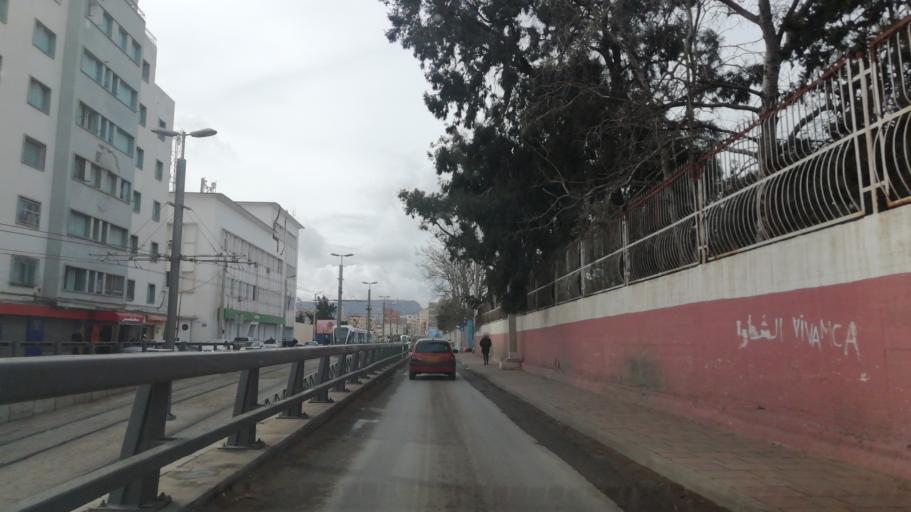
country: DZ
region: Oran
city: Oran
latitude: 35.6974
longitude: -0.6146
